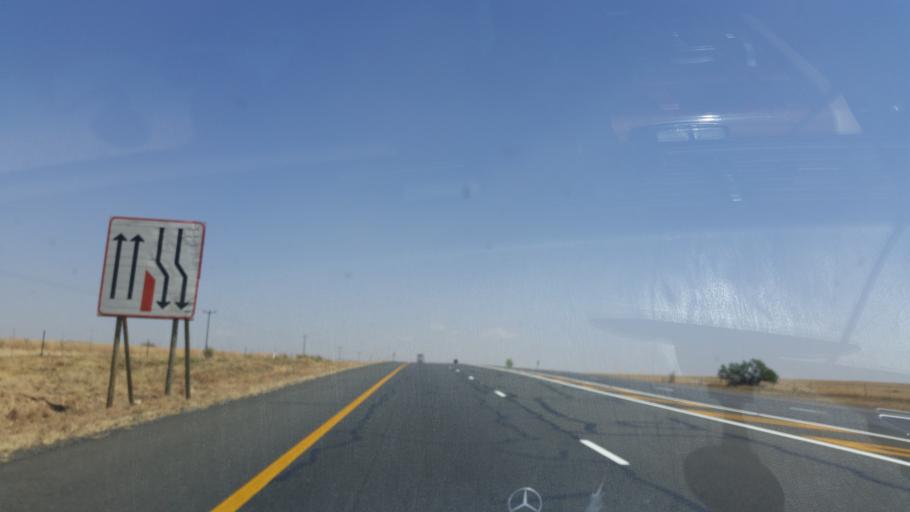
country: ZA
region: Orange Free State
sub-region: Lejweleputswa District Municipality
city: Brandfort
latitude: -28.8541
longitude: 26.5657
